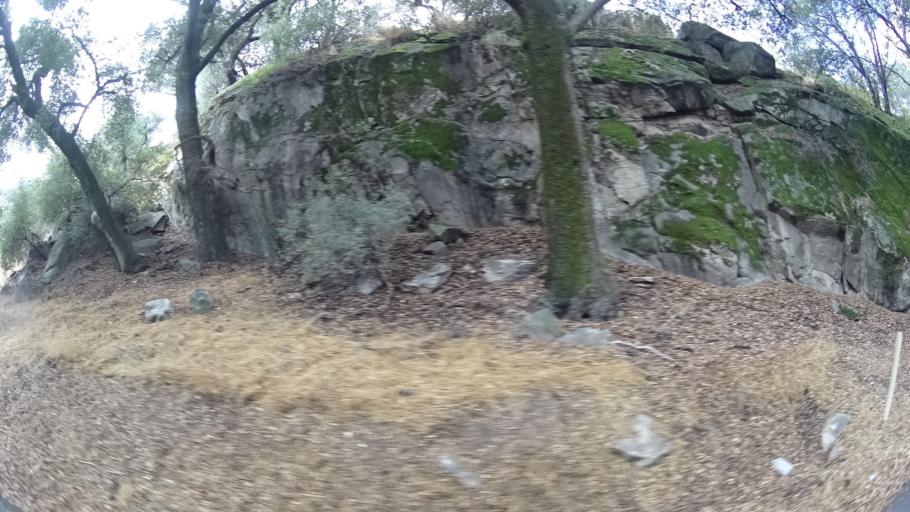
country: US
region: California
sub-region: San Diego County
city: Campo
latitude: 32.6080
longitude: -116.4796
